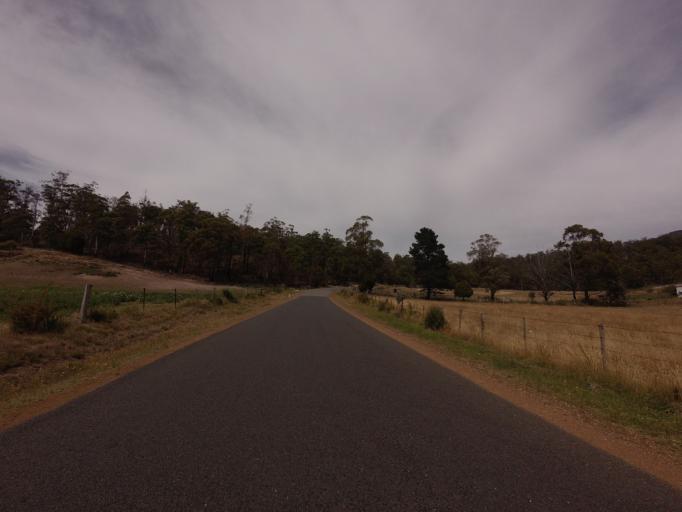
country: AU
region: Tasmania
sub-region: Sorell
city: Sorell
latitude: -42.5782
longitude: 147.5596
